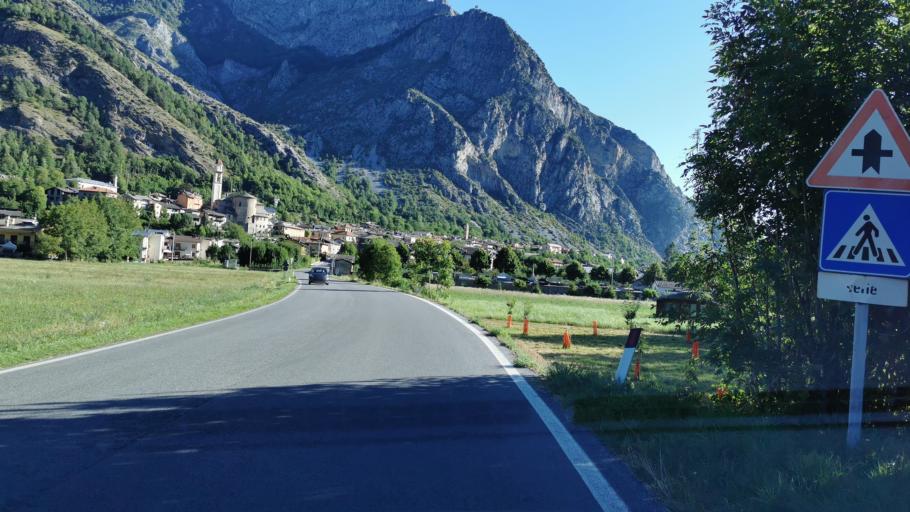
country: IT
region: Piedmont
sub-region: Provincia di Cuneo
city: Valdieri
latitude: 44.2728
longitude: 7.3962
